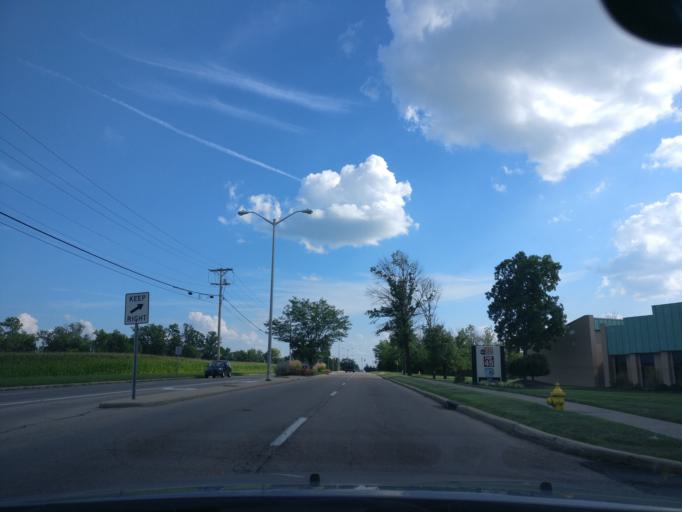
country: US
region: Ohio
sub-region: Montgomery County
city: West Carrollton City
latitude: 39.6364
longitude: -84.2347
